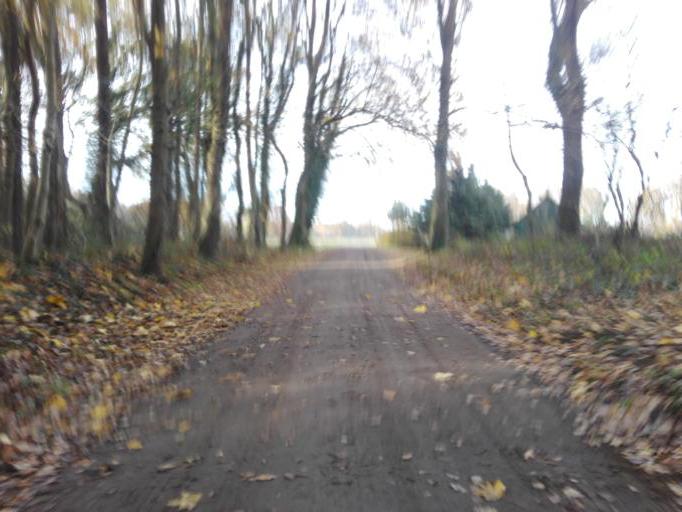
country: DE
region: Lower Saxony
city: Wiefelstede
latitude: 53.2756
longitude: 8.1545
